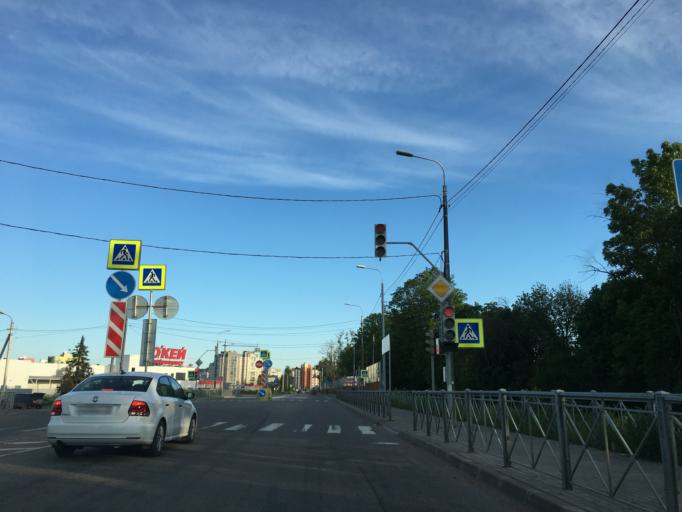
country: RU
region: Leningrad
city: Gatchina
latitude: 59.5855
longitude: 30.1363
